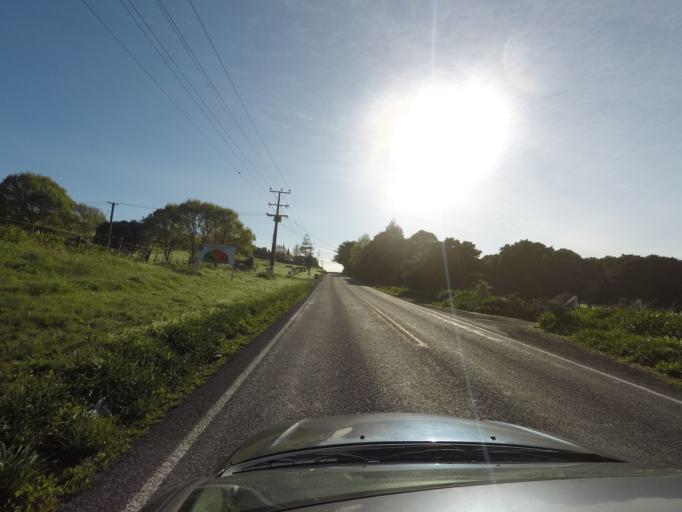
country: NZ
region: Auckland
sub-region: Auckland
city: Red Hill
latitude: -37.0143
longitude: 174.9458
